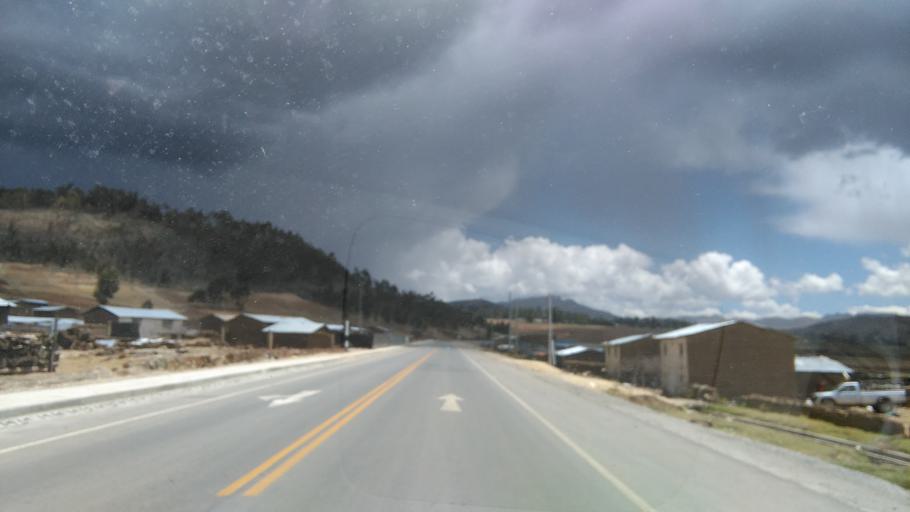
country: PE
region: Apurimac
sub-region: Provincia de Andahuaylas
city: San Jeronimo
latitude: -13.7139
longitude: -73.3502
